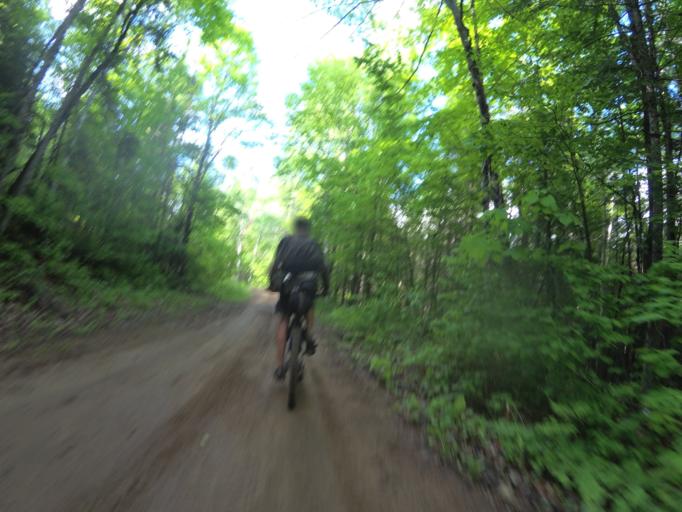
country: CA
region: Ontario
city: Renfrew
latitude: 45.1632
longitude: -76.9588
